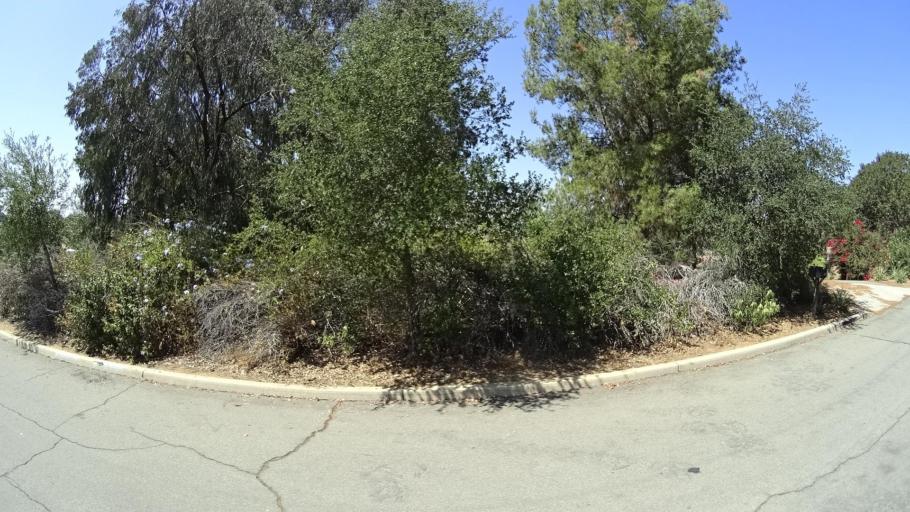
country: US
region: California
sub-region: San Diego County
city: Fallbrook
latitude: 33.3926
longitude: -117.2471
